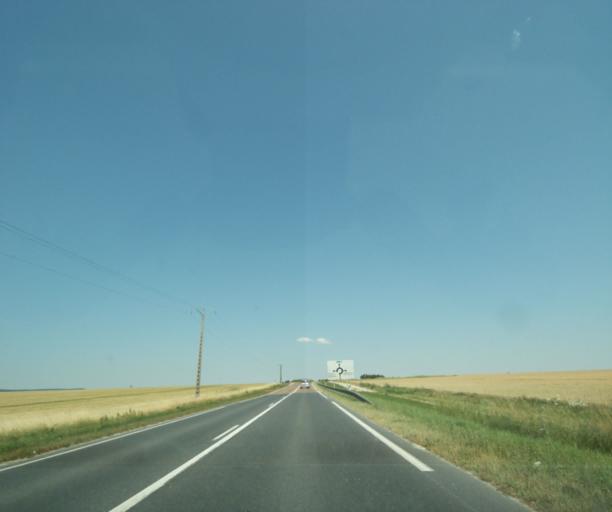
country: FR
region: Champagne-Ardenne
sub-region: Departement de la Marne
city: Mourmelon-le-Grand
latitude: 49.0962
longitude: 4.2691
